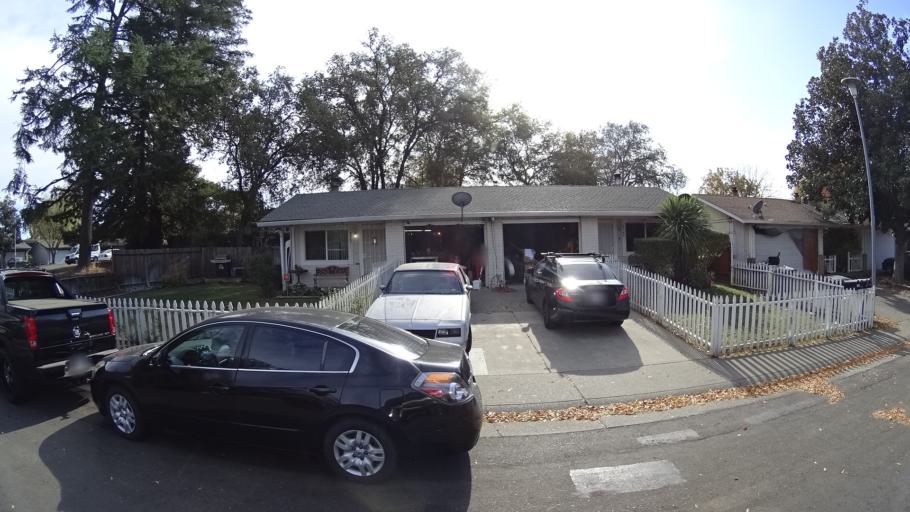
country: US
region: California
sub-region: Sacramento County
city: Citrus Heights
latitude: 38.6827
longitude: -121.2746
